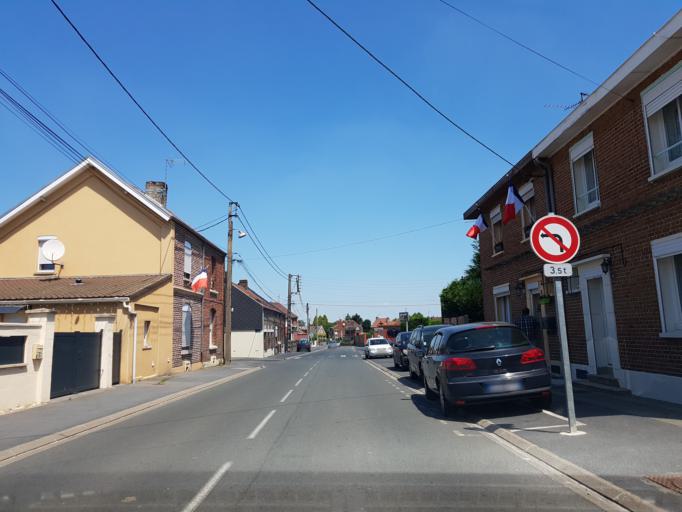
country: FR
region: Nord-Pas-de-Calais
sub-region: Departement du Nord
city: Neuville-sur-Escaut
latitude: 50.2964
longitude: 3.3567
